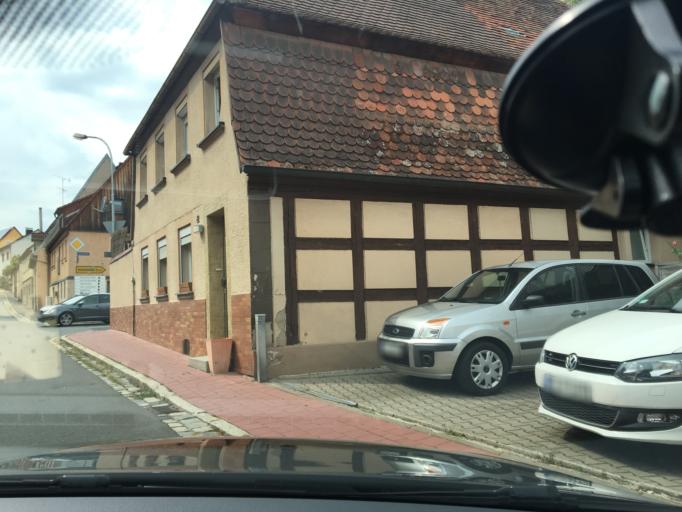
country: DE
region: Bavaria
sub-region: Regierungsbezirk Mittelfranken
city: Wilhermsdorf
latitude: 49.4819
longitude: 10.7134
